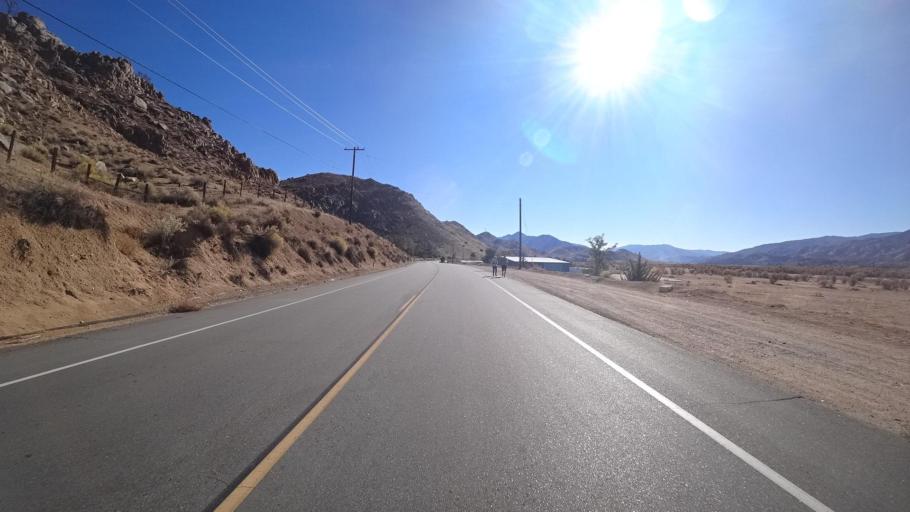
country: US
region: California
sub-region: Kern County
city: Kernville
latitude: 35.7240
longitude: -118.4170
